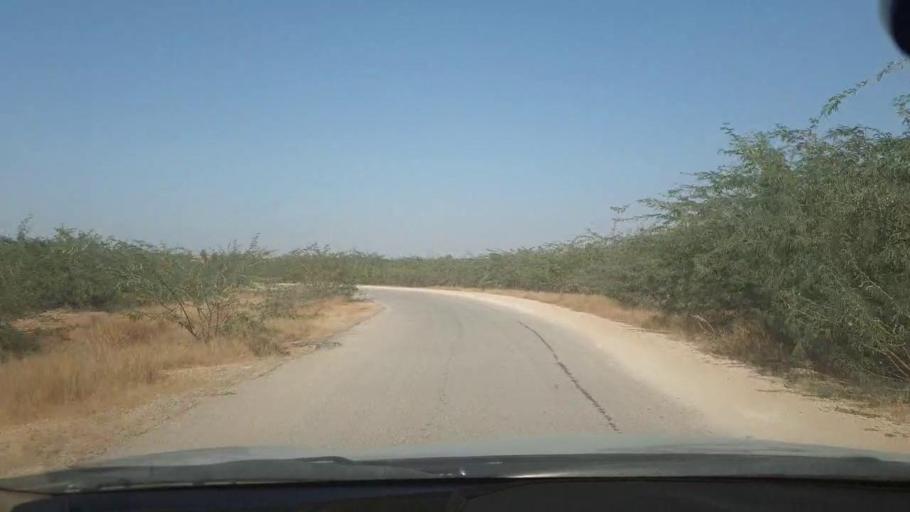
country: PK
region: Sindh
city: Malir Cantonment
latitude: 25.1460
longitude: 67.1664
